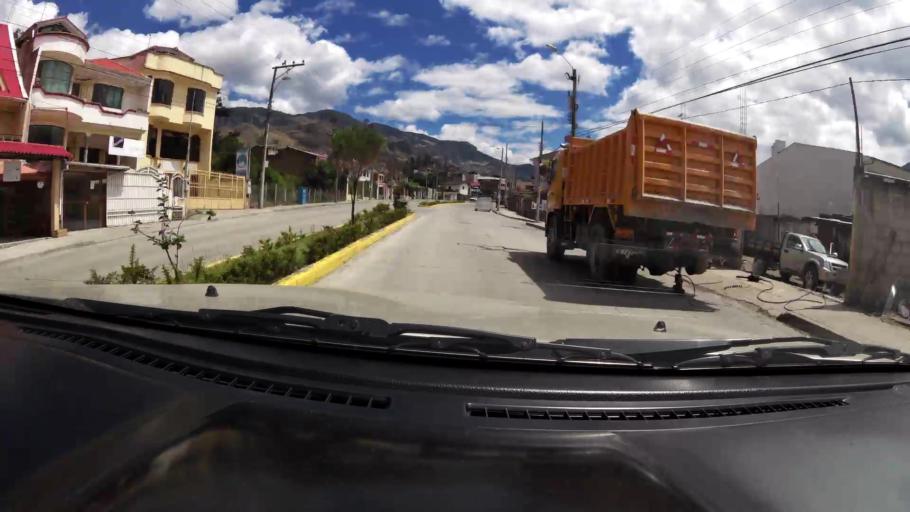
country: EC
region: Azuay
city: Cuenca
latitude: -3.1603
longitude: -79.1509
